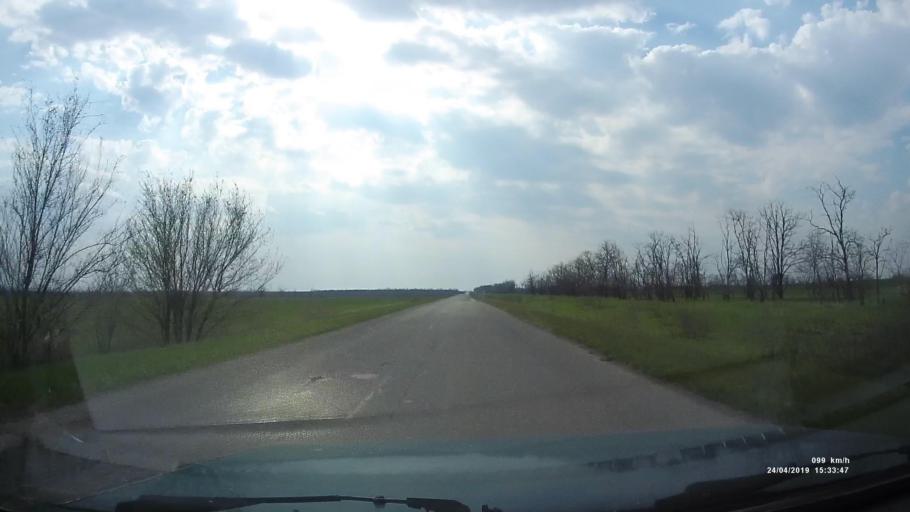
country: RU
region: Kalmykiya
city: Yashalta
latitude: 46.5989
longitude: 42.9303
